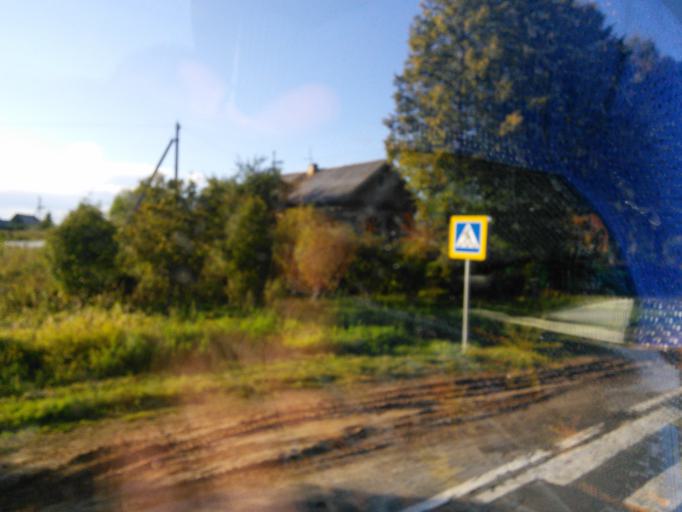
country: RU
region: Jaroslavl
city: Poshekhon'ye
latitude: 58.4579
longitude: 39.0397
